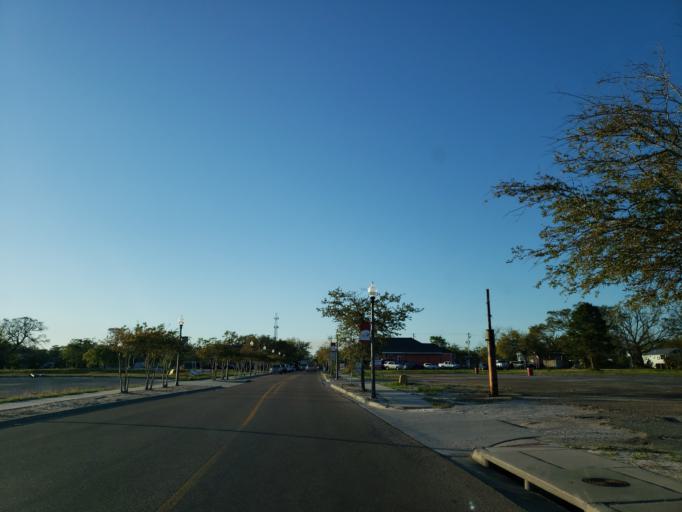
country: US
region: Mississippi
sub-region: Harrison County
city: Long Beach
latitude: 30.3454
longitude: -89.1482
